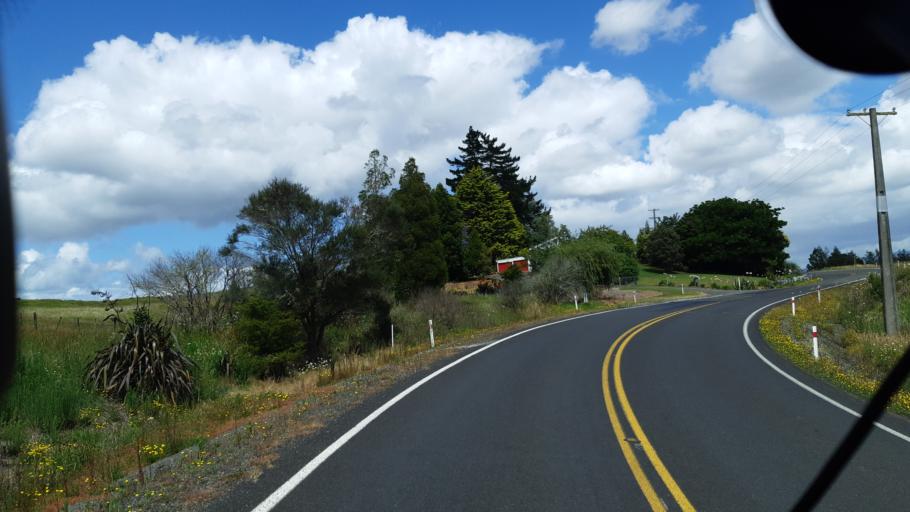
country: NZ
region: Northland
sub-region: Far North District
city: Waimate North
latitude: -35.3015
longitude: 173.5995
